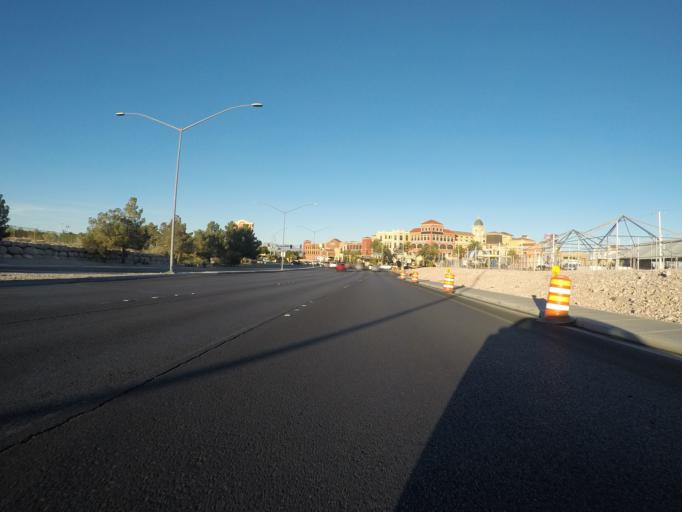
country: US
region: Nevada
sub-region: Clark County
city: Summerlin South
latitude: 36.1658
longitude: -115.2889
